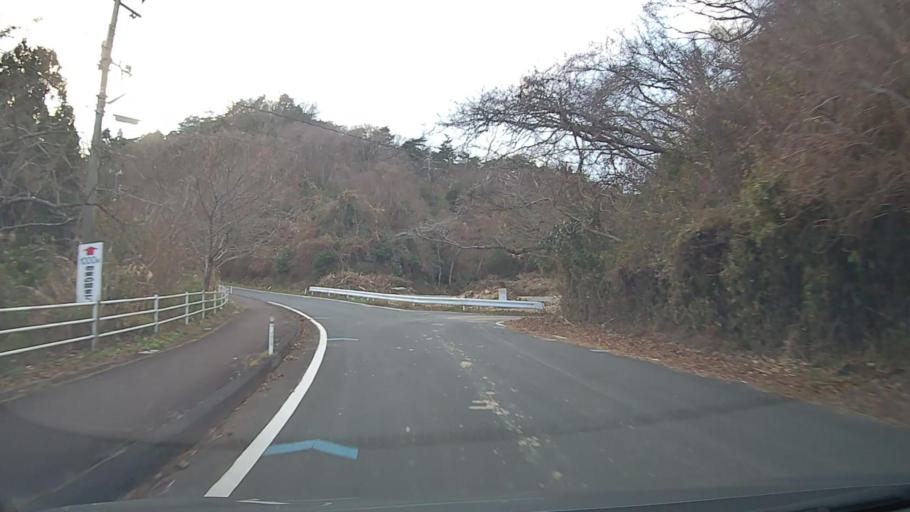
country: JP
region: Ibaraki
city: Kitaibaraki
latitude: 36.8680
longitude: 140.7844
